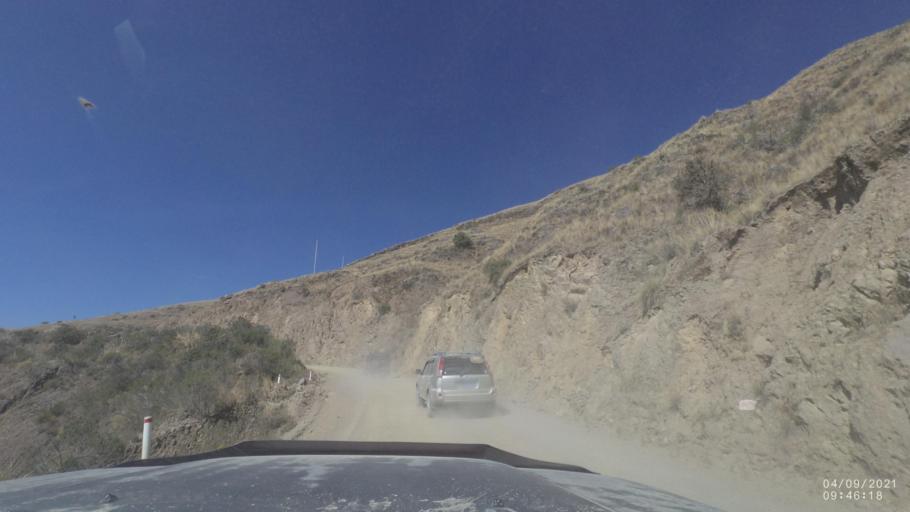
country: BO
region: Cochabamba
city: Sipe Sipe
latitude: -17.3499
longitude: -66.3887
